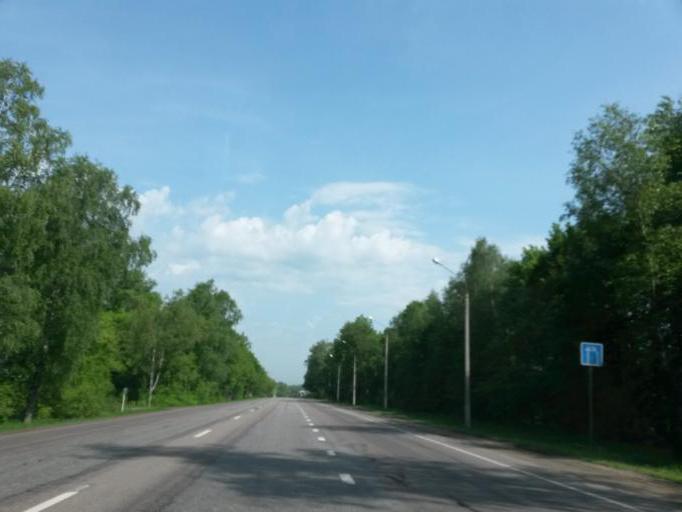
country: RU
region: Moskovskaya
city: Stolbovaya
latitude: 55.2110
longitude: 37.5065
